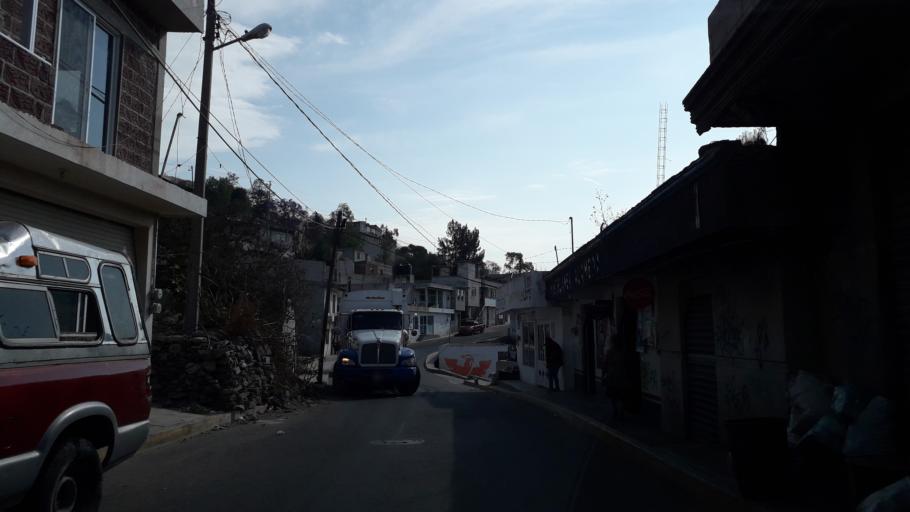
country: MX
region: Puebla
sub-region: Puebla
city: San Andres Azumiatla
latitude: 18.9043
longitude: -98.2532
